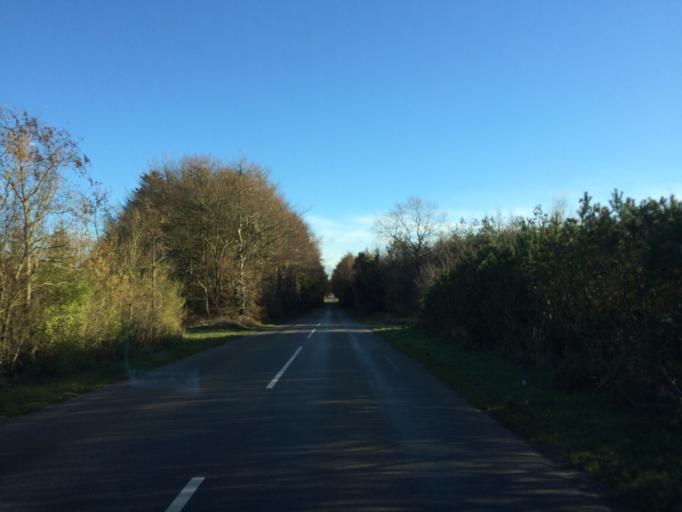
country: DK
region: Central Jutland
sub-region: Herning Kommune
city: Kibaek
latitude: 56.0559
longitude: 8.7814
